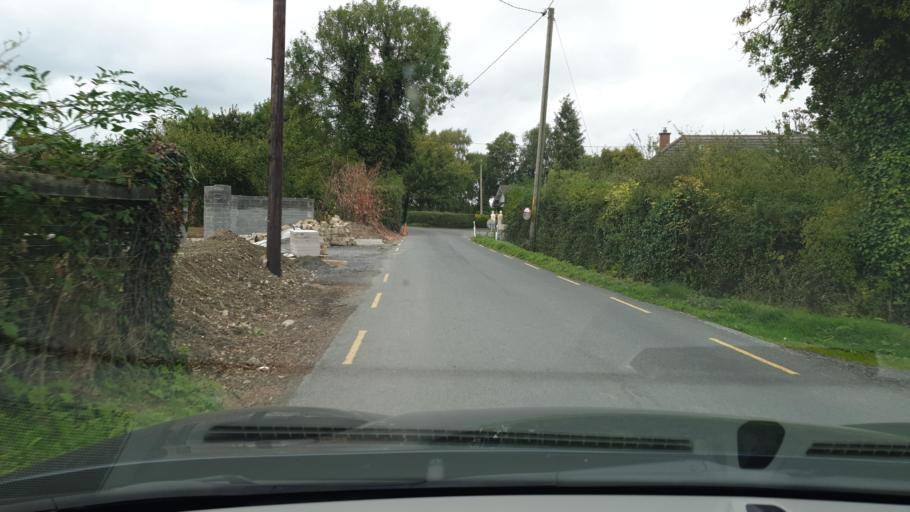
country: IE
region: Leinster
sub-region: Kildare
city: Clane
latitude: 53.2993
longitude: -6.7128
